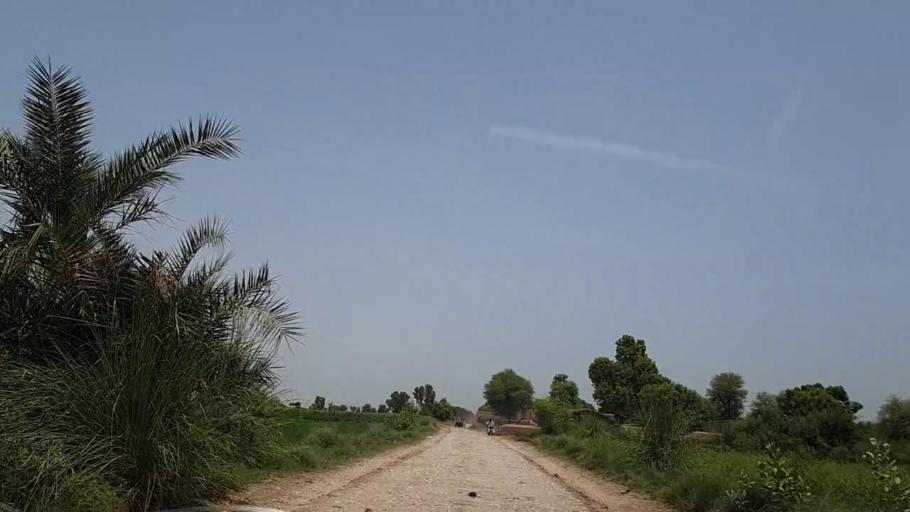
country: PK
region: Sindh
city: Tharu Shah
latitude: 26.9636
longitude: 68.0332
